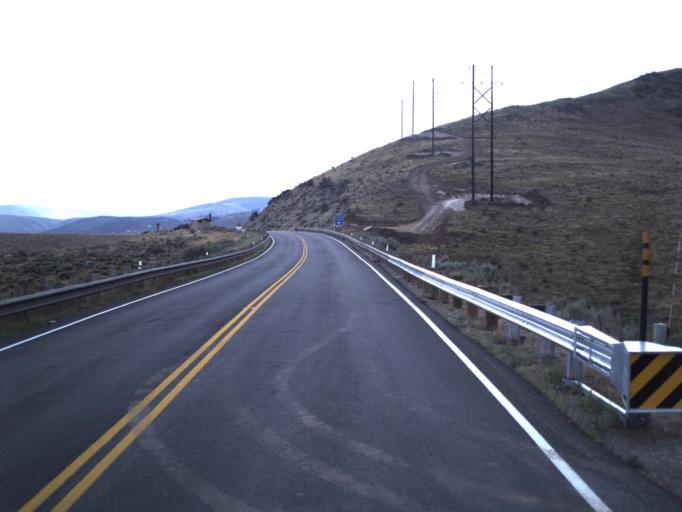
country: US
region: Utah
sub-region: Summit County
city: Coalville
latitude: 40.7887
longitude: -111.4097
